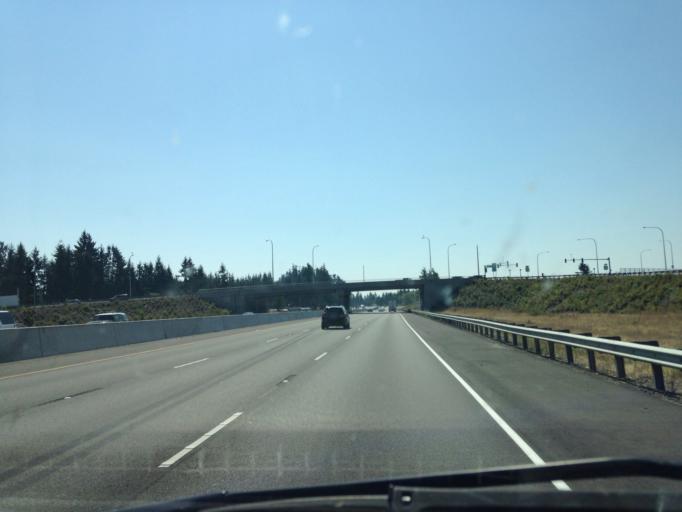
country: US
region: Washington
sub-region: Thurston County
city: Grand Mound
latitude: 46.8044
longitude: -123.0062
